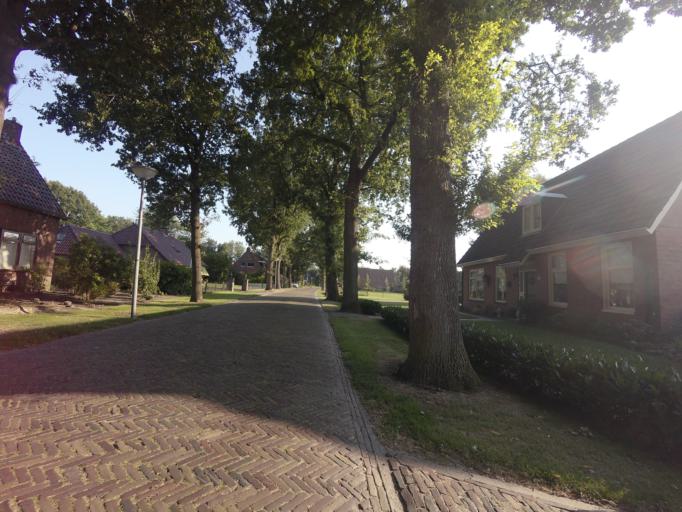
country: NL
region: Groningen
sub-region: Gemeente Groningen
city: Groningen
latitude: 53.1450
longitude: 6.4886
